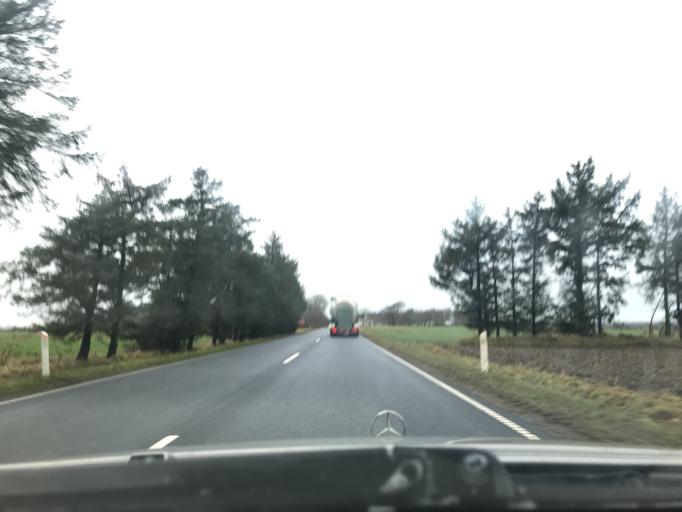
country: DK
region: South Denmark
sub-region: Esbjerg Kommune
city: Ribe
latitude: 55.2756
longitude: 8.8642
